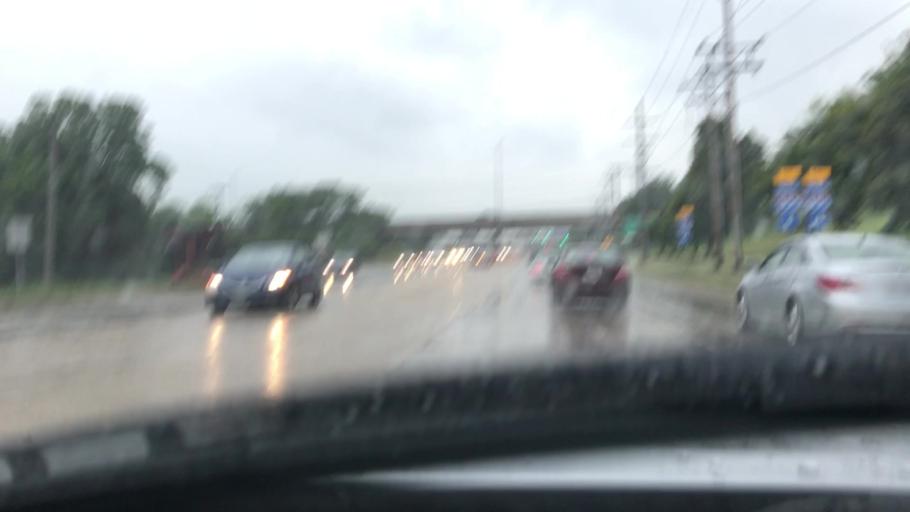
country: US
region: Illinois
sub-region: DuPage County
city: Lisle
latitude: 41.8043
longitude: -88.0515
